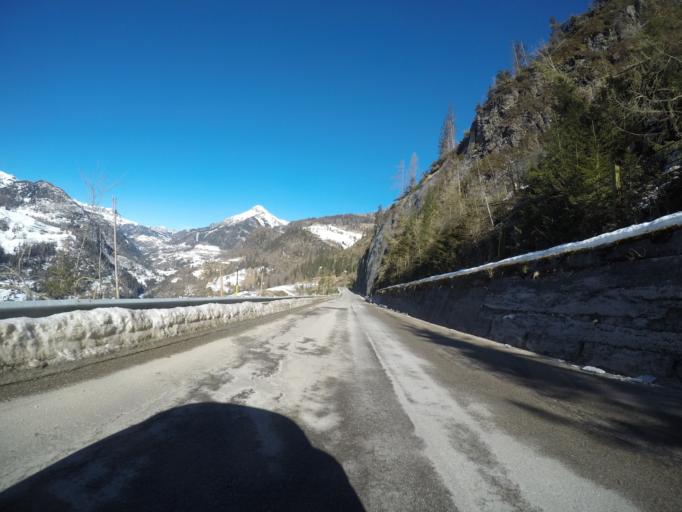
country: IT
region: Veneto
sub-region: Provincia di Belluno
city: Colle Santa Lucia
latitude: 46.4495
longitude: 11.9937
